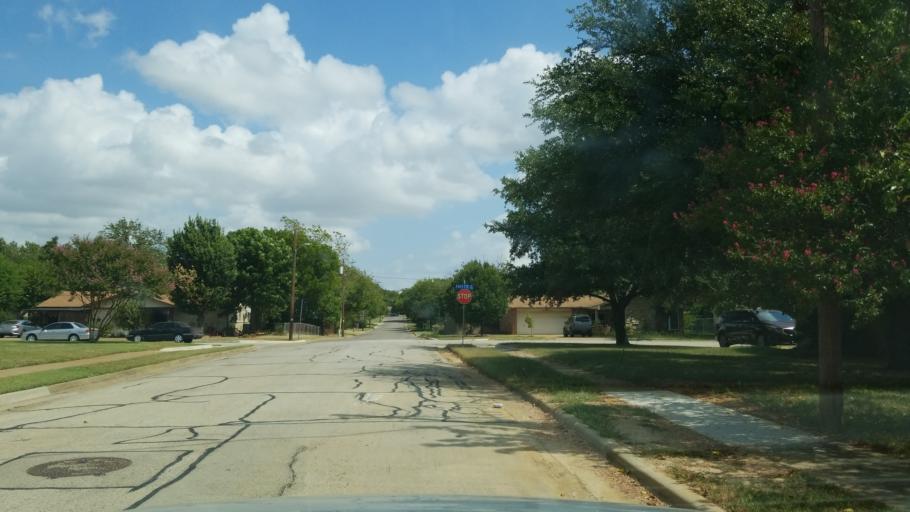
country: US
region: Texas
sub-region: Tarrant County
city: Euless
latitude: 32.8481
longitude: -97.0950
